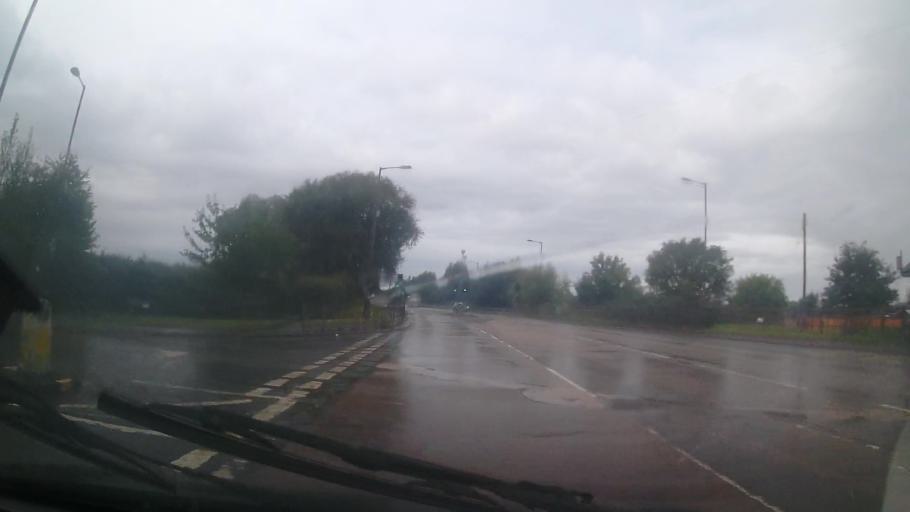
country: GB
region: England
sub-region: Worcestershire
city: Pershore
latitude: 52.1256
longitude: -2.0303
